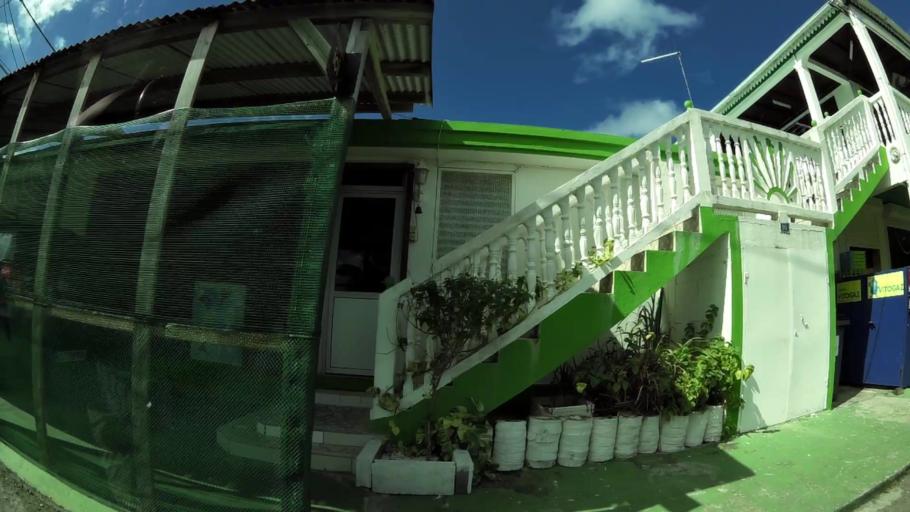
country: GP
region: Guadeloupe
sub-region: Guadeloupe
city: Port-Louis
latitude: 16.4202
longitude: -61.5297
